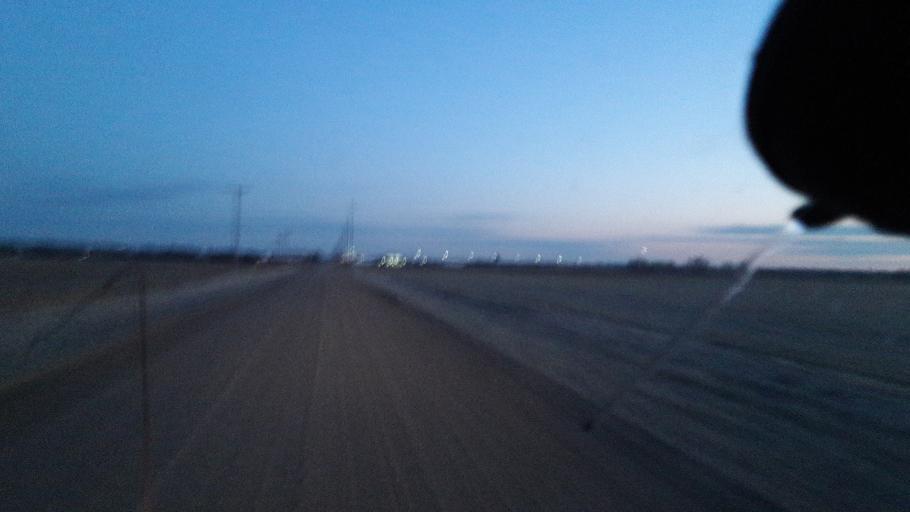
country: US
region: Kansas
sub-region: Reno County
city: South Hutchinson
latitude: 38.0102
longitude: -97.9768
